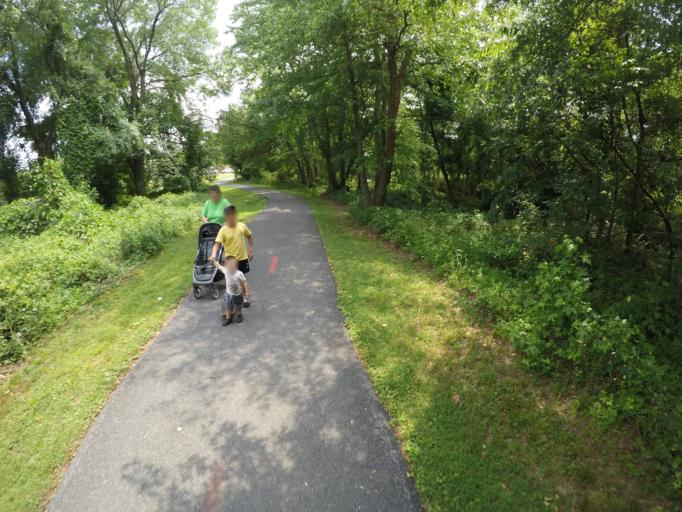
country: US
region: Maryland
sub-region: Prince George's County
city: Chillum
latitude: 38.9617
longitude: -76.9716
